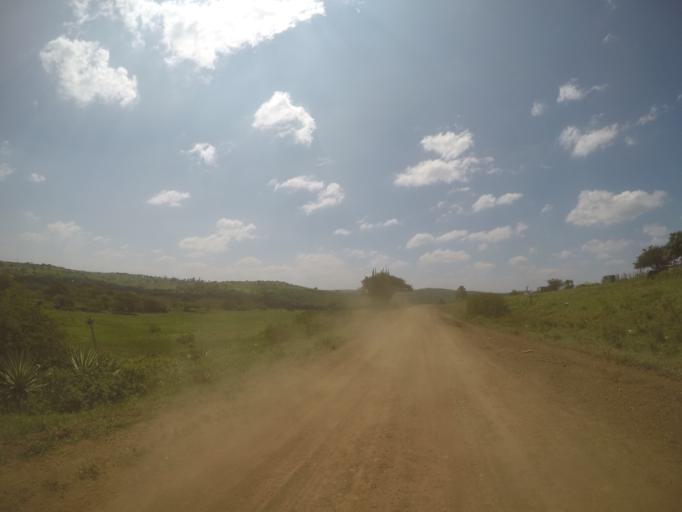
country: ZA
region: KwaZulu-Natal
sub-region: uThungulu District Municipality
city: Empangeni
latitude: -28.5918
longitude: 31.7363
